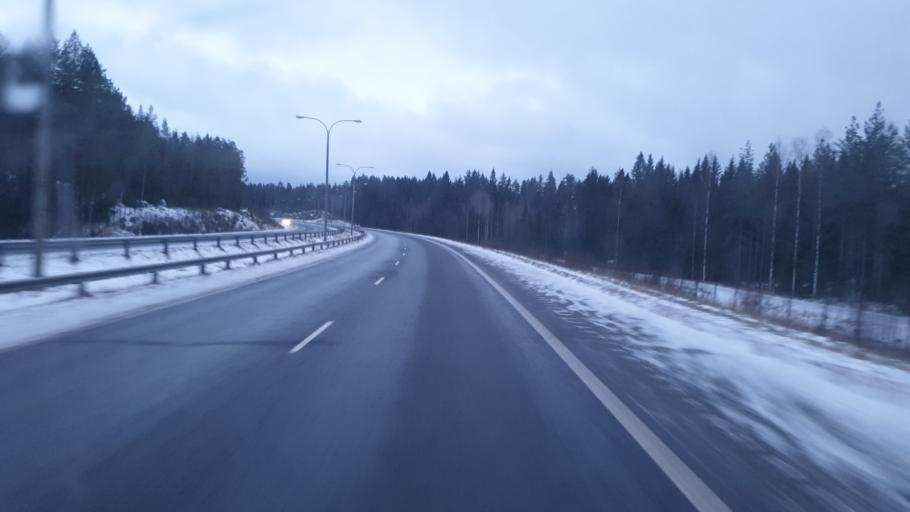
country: FI
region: Northern Savo
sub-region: Kuopio
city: Siilinjaervi
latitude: 63.0056
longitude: 27.6807
